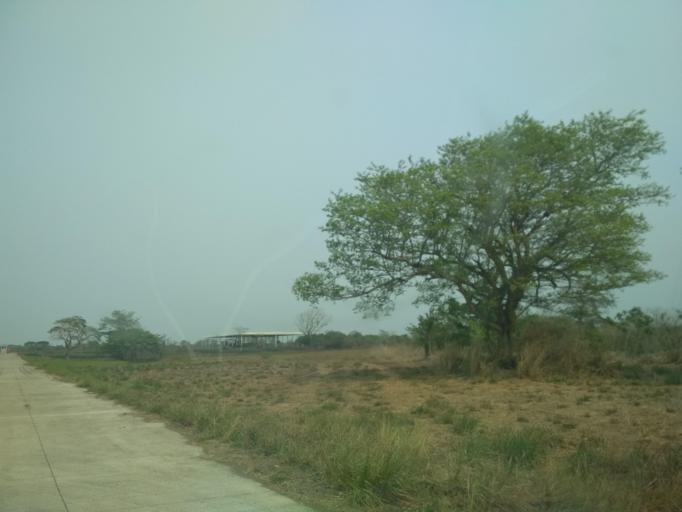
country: MX
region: Veracruz
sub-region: Veracruz
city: Delfino Victoria (Santa Fe)
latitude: 19.2137
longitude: -96.3122
